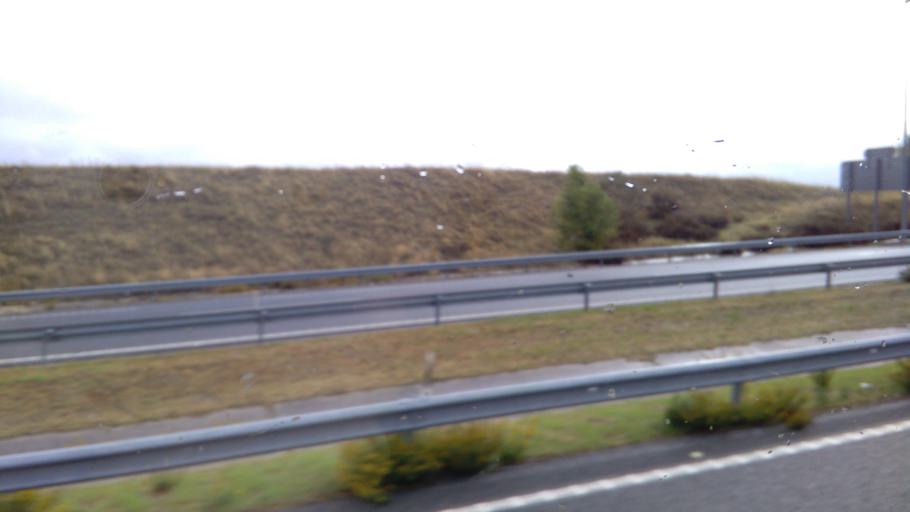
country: ES
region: Madrid
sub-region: Provincia de Madrid
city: Alcorcon
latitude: 40.3295
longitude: -3.8151
